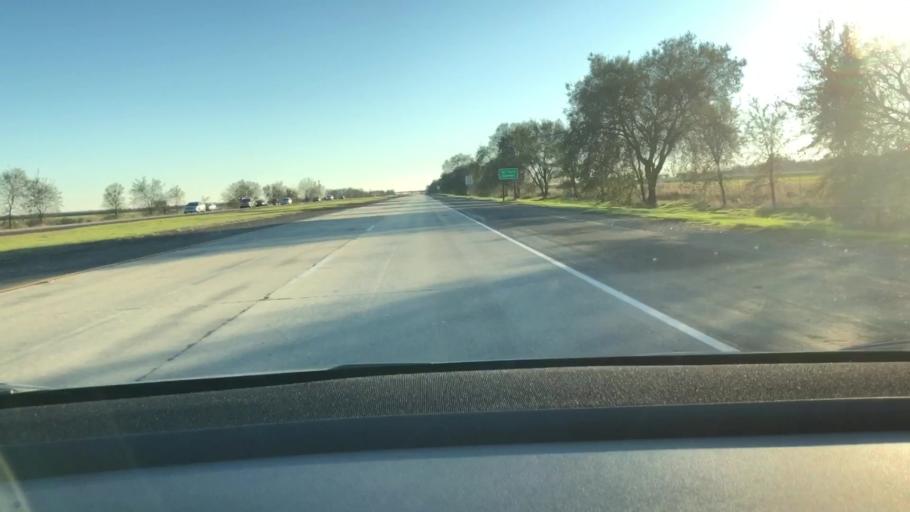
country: US
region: California
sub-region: Yolo County
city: Woodland
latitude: 38.6538
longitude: -121.7547
